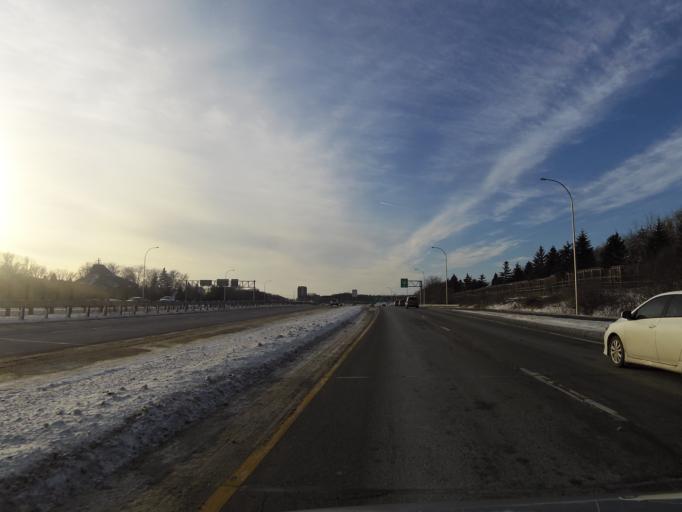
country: US
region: Minnesota
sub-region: Hennepin County
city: Edina
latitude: 44.8901
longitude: -93.3908
